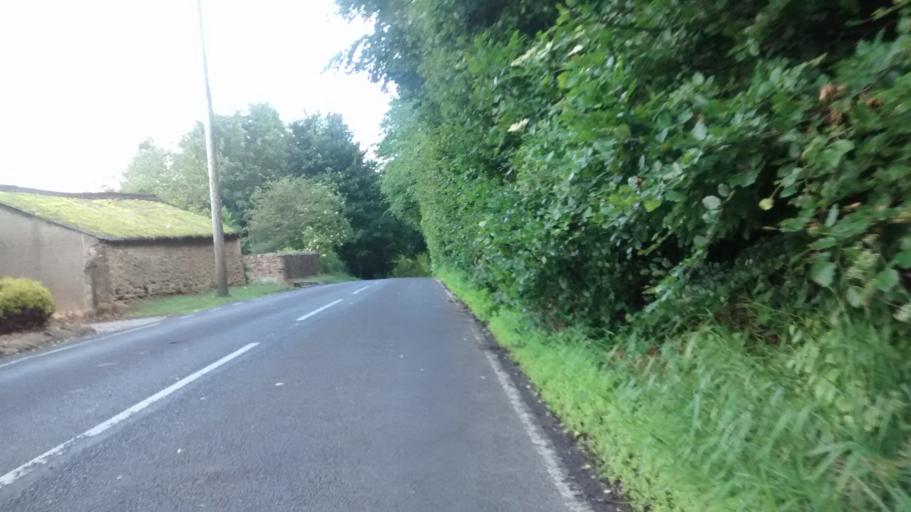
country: GB
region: England
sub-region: County Durham
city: Chester-le-Street
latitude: 54.8271
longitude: -1.5725
